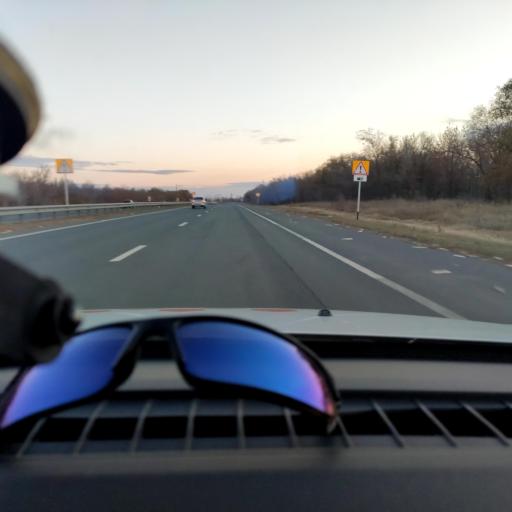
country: RU
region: Samara
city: Novokuybyshevsk
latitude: 53.0442
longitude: 50.0049
